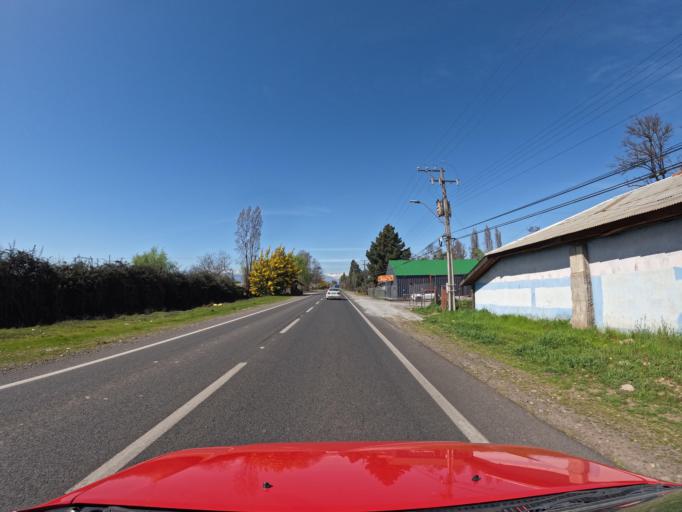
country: CL
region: Maule
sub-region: Provincia de Curico
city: Teno
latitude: -34.9626
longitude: -71.0792
